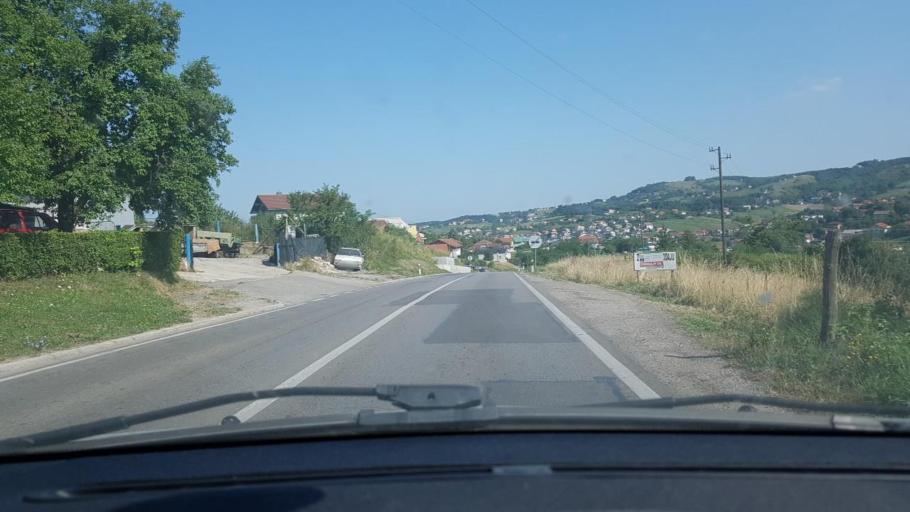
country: BA
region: Federation of Bosnia and Herzegovina
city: Cazin
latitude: 44.9590
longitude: 15.9290
